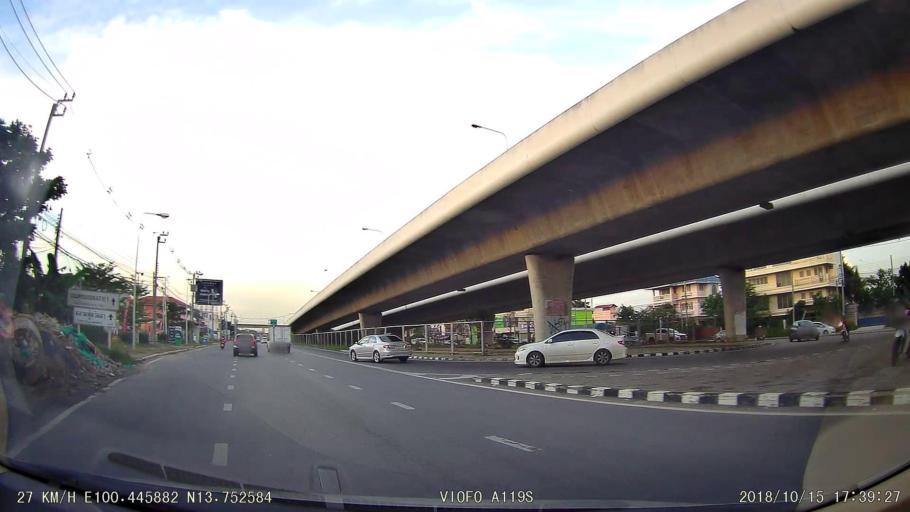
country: TH
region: Bangkok
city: Taling Chan
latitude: 13.7528
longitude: 100.4460
